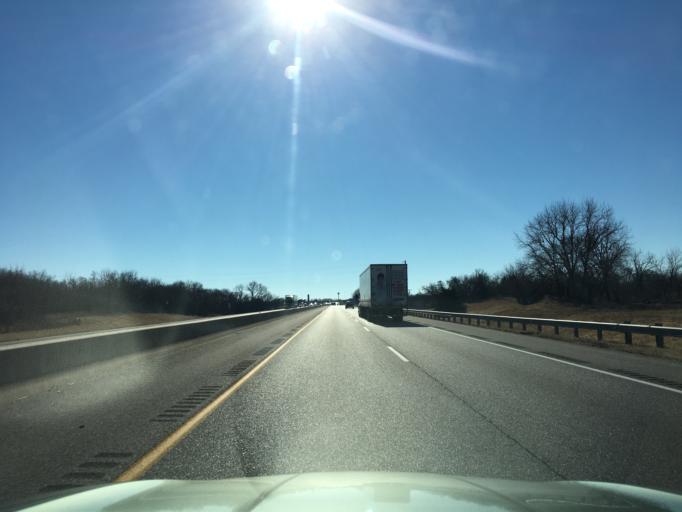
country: US
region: Kansas
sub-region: Sumner County
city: Belle Plaine
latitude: 37.3862
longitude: -97.3248
